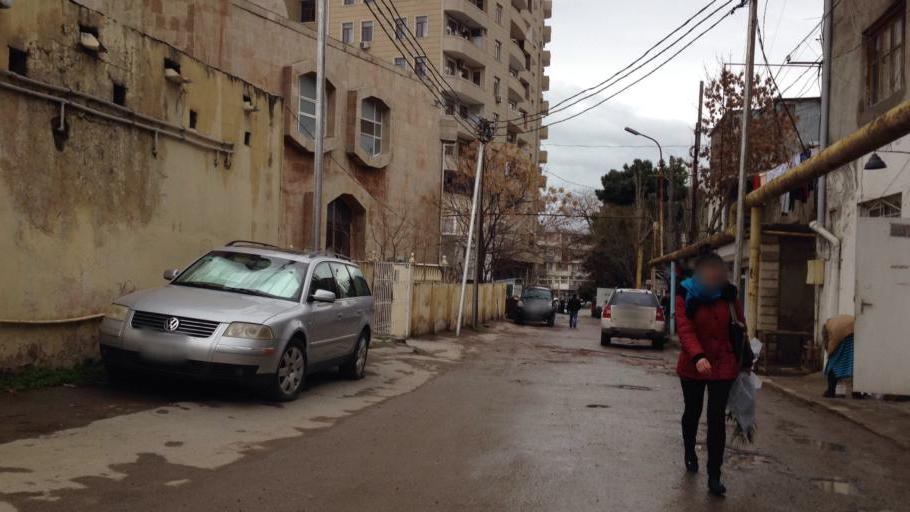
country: AZ
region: Baki
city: Baku
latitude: 40.3861
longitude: 49.8501
